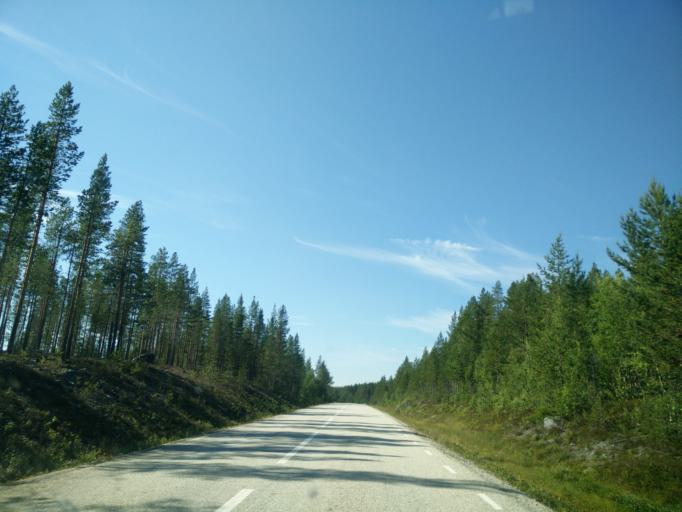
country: SE
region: Jaemtland
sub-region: Are Kommun
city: Jarpen
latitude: 62.8241
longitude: 13.4954
